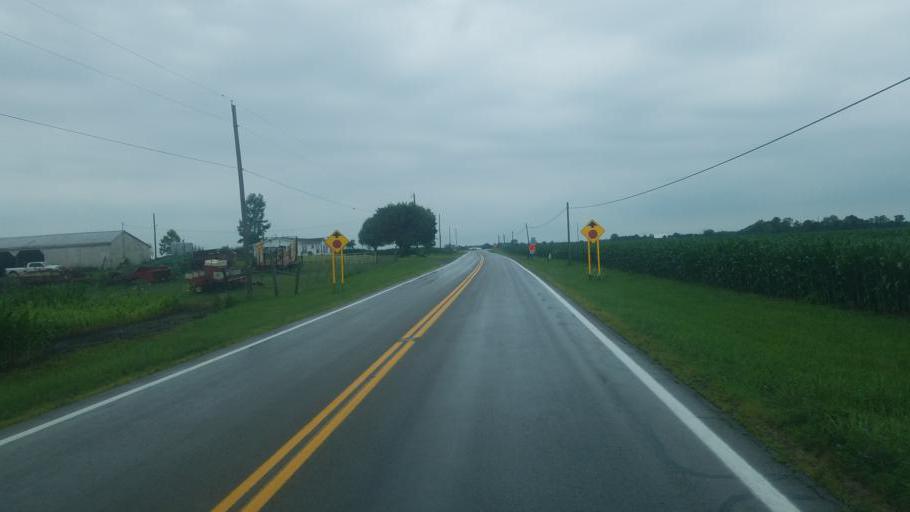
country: US
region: Ohio
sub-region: Hardin County
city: Kenton
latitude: 40.5286
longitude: -83.5718
